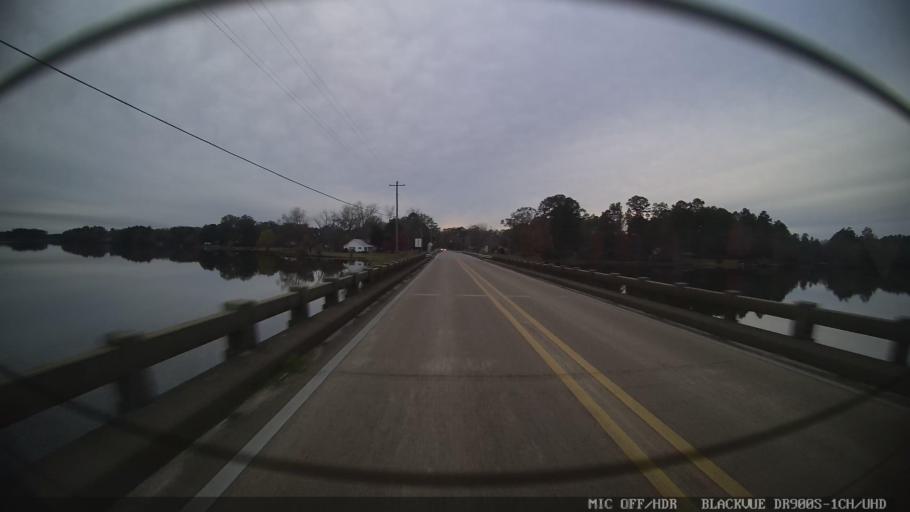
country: US
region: Mississippi
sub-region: Clarke County
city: Quitman
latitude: 32.0395
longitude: -88.7109
